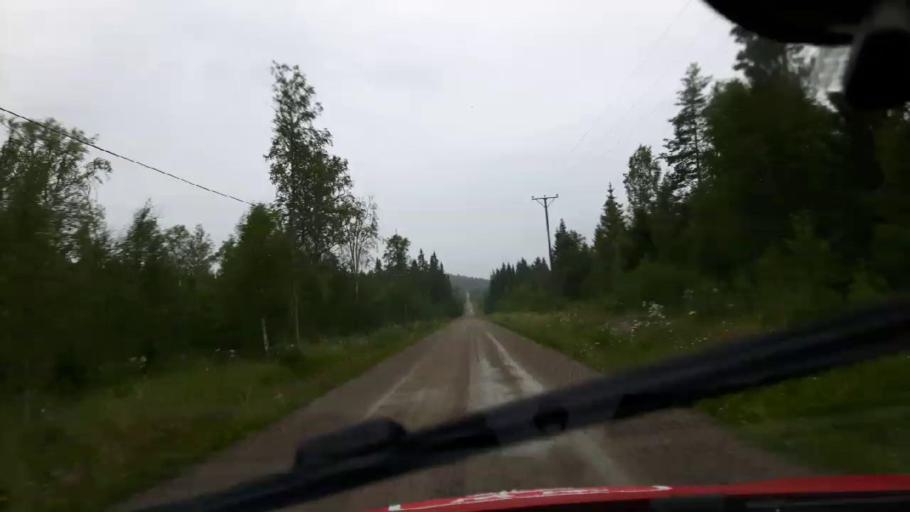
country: SE
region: Jaemtland
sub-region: OEstersunds Kommun
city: Brunflo
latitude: 62.7758
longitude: 14.9880
